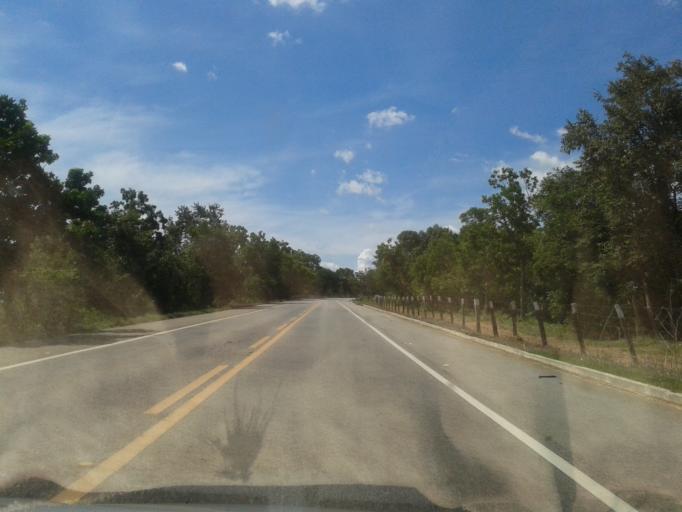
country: BR
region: Goias
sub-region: Goias
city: Goias
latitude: -15.7411
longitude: -50.1808
